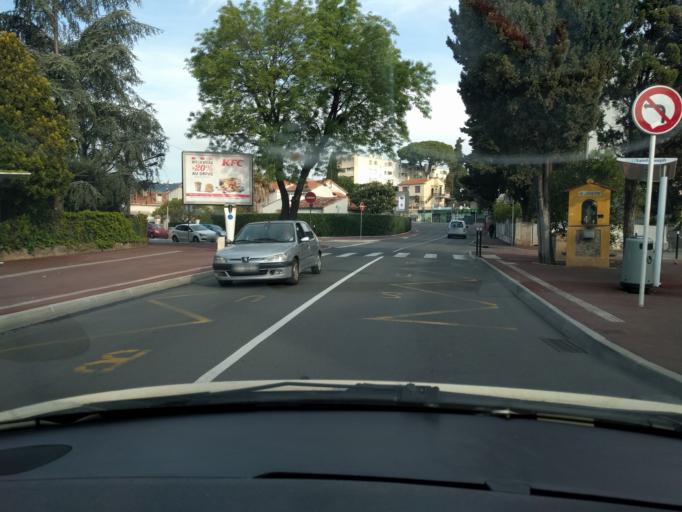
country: FR
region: Provence-Alpes-Cote d'Azur
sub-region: Departement des Alpes-Maritimes
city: Mandelieu-la-Napoule
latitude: 43.5547
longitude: 6.9724
